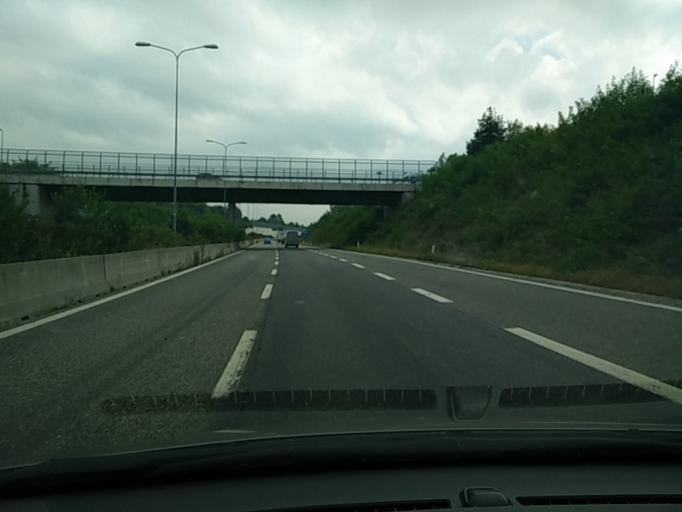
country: IT
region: Lombardy
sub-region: Provincia di Varese
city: Vizzola Ticino
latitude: 45.6206
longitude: 8.7069
